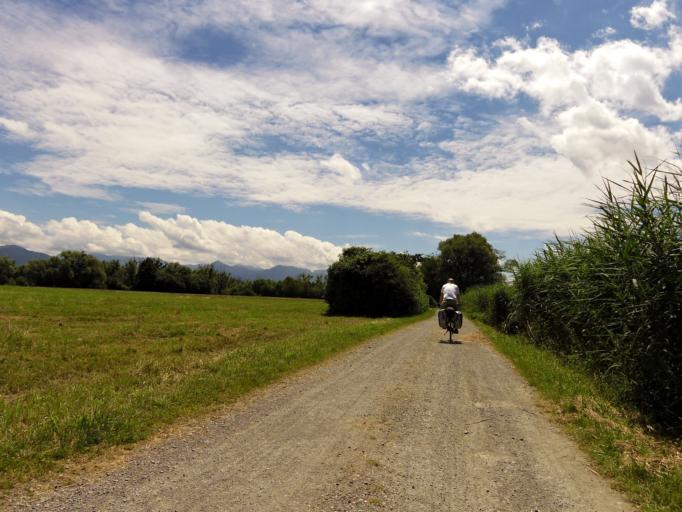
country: AT
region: Vorarlberg
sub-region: Politischer Bezirk Bregenz
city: Hard
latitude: 47.4926
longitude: 9.6757
